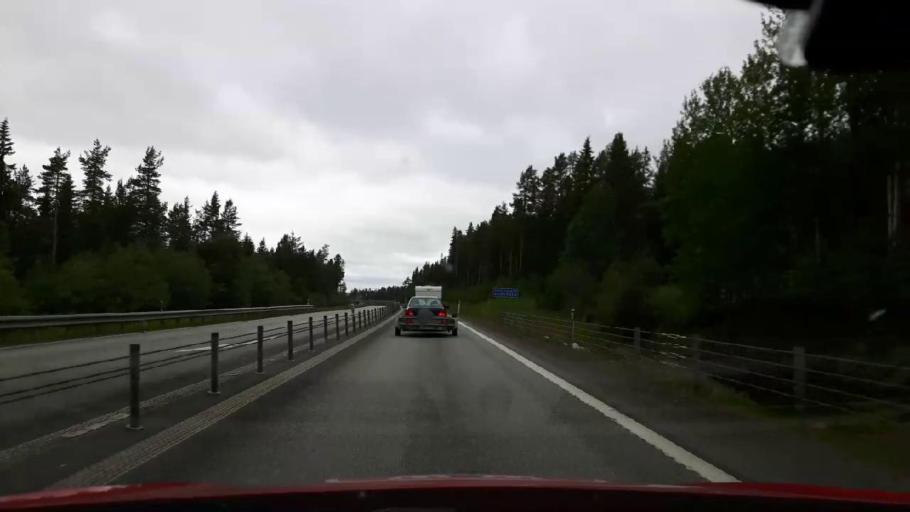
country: SE
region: Jaemtland
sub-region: OEstersunds Kommun
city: Ostersund
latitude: 63.1991
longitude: 14.6836
